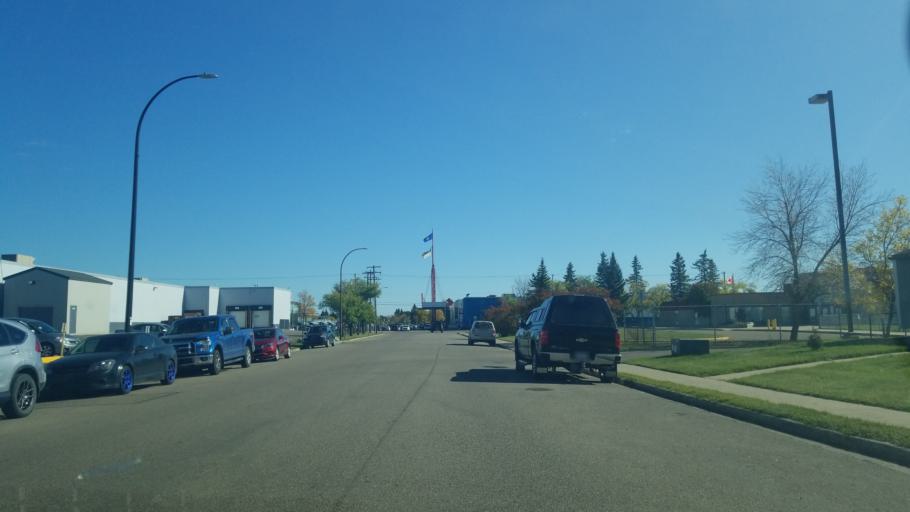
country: CA
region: Saskatchewan
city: Lloydminster
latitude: 53.2761
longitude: -110.0122
